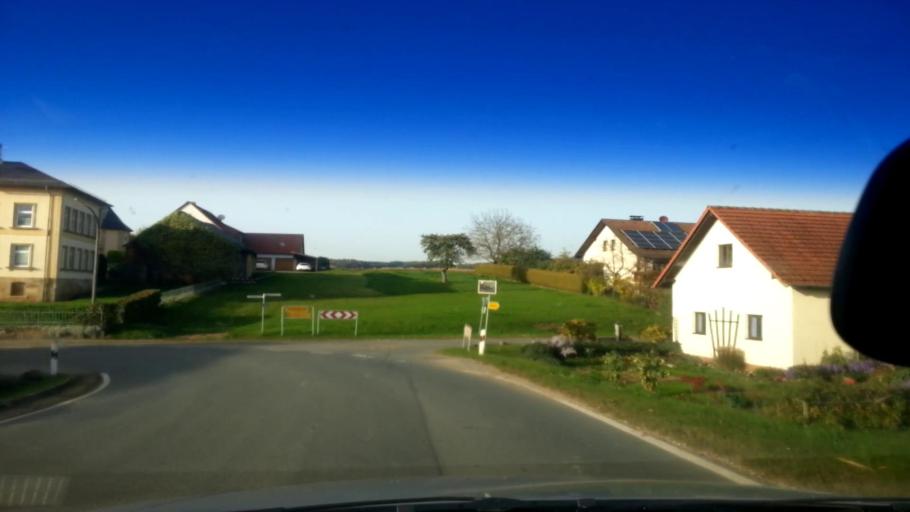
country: DE
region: Bavaria
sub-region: Upper Franconia
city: Schesslitz
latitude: 50.0032
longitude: 11.0189
